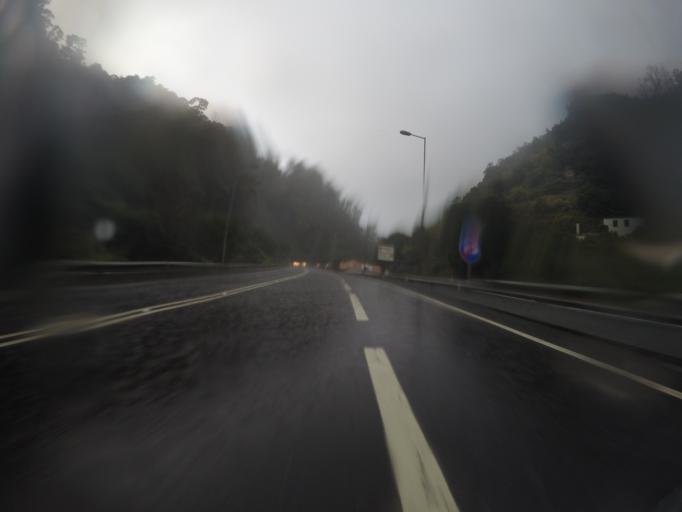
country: PT
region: Madeira
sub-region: Machico
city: Machico
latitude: 32.7349
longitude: -16.8030
